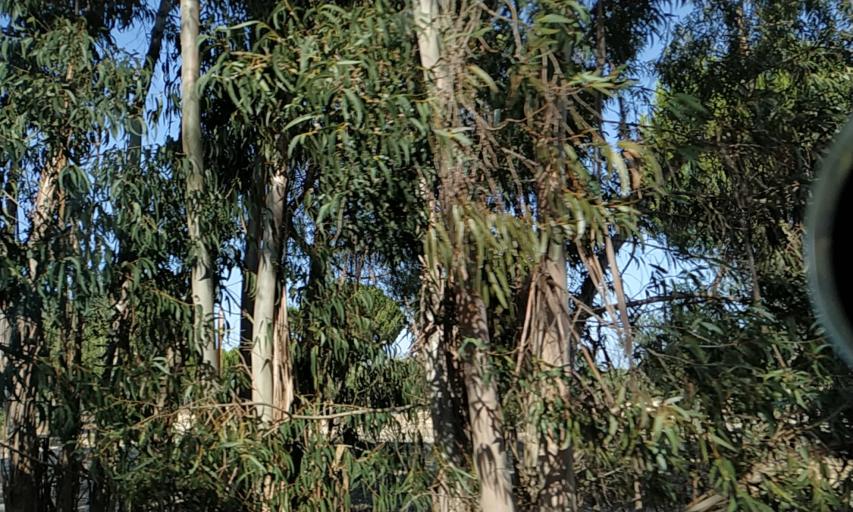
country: PT
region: Santarem
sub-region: Coruche
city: Coruche
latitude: 38.8055
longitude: -8.5790
